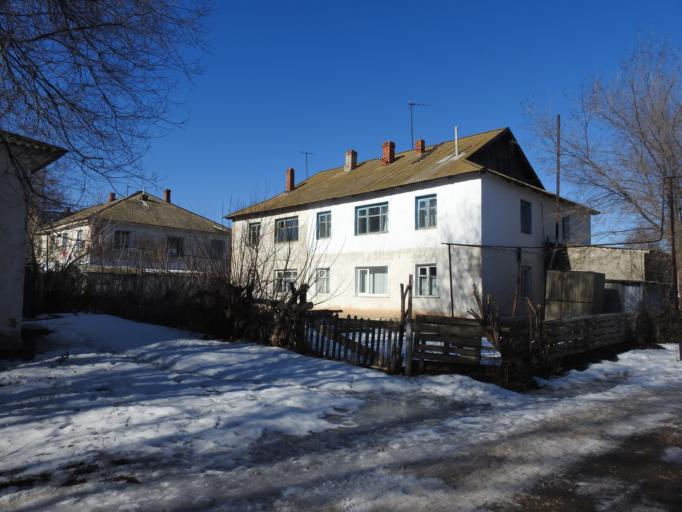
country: RU
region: Saratov
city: Yershov
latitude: 51.3408
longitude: 48.2243
